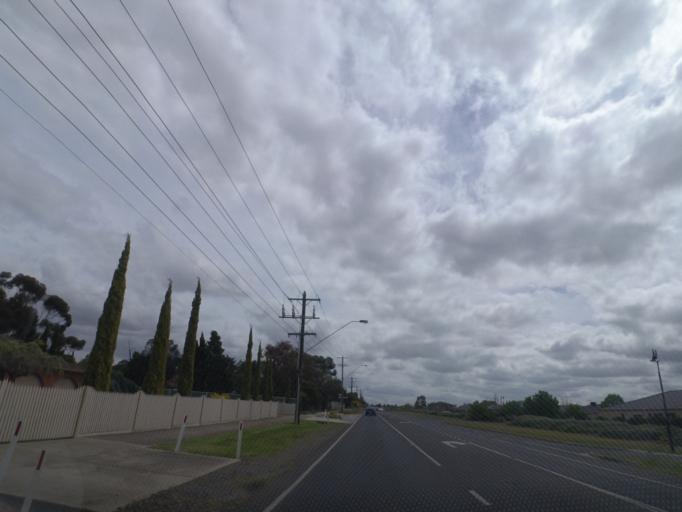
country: AU
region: Victoria
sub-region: Wyndham
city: Hoppers Crossing
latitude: -37.8495
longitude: 144.6971
